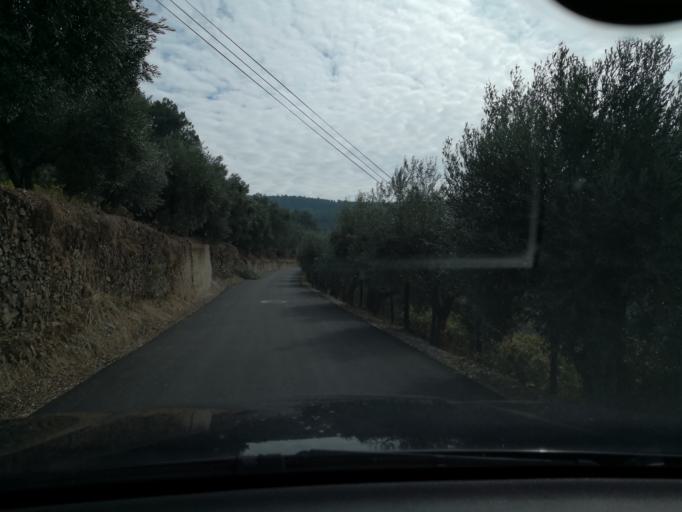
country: PT
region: Vila Real
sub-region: Sabrosa
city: Vilela
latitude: 41.2170
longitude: -7.6861
